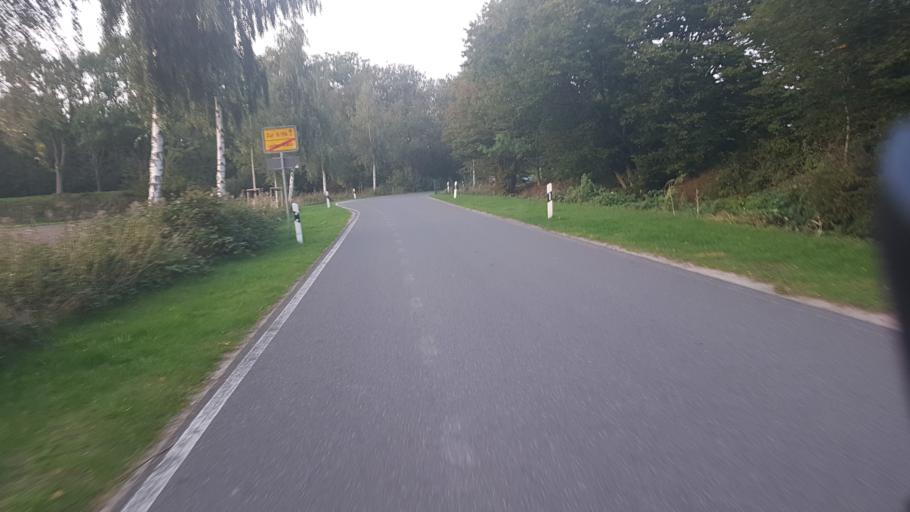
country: DE
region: Mecklenburg-Vorpommern
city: Ostseebad Binz
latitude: 54.3676
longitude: 13.6280
